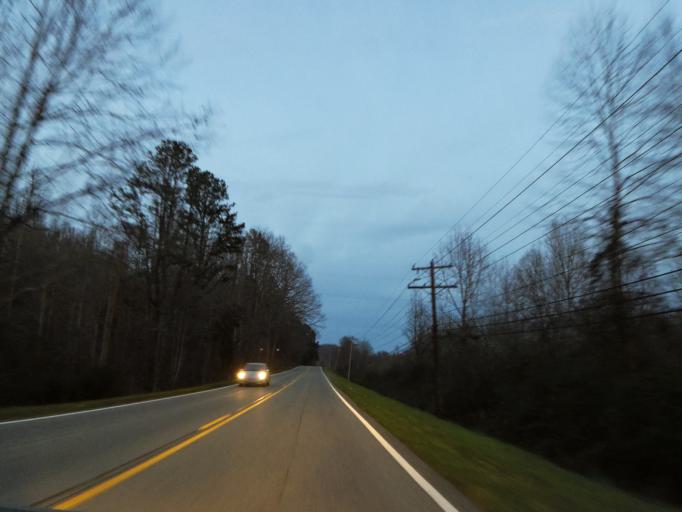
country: US
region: Tennessee
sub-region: Morgan County
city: Coalfield
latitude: 35.9753
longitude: -84.4571
